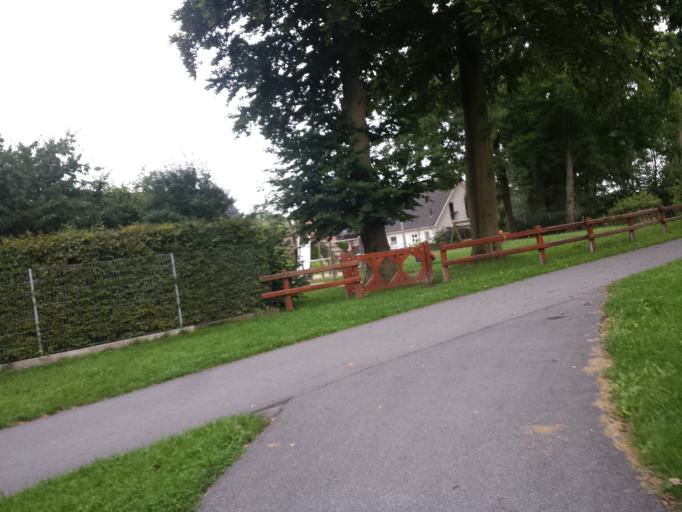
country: DE
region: North Rhine-Westphalia
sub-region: Regierungsbezirk Detmold
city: Harsewinkel
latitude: 51.9708
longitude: 8.2428
